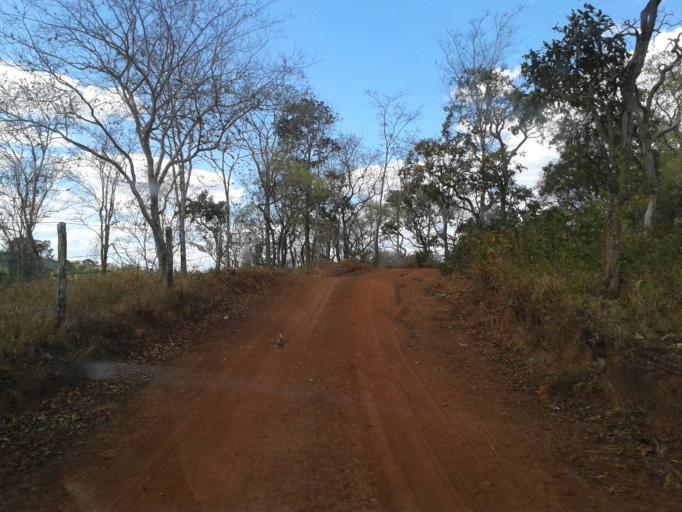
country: BR
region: Minas Gerais
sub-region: Monte Alegre De Minas
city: Monte Alegre de Minas
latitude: -18.7947
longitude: -49.0923
